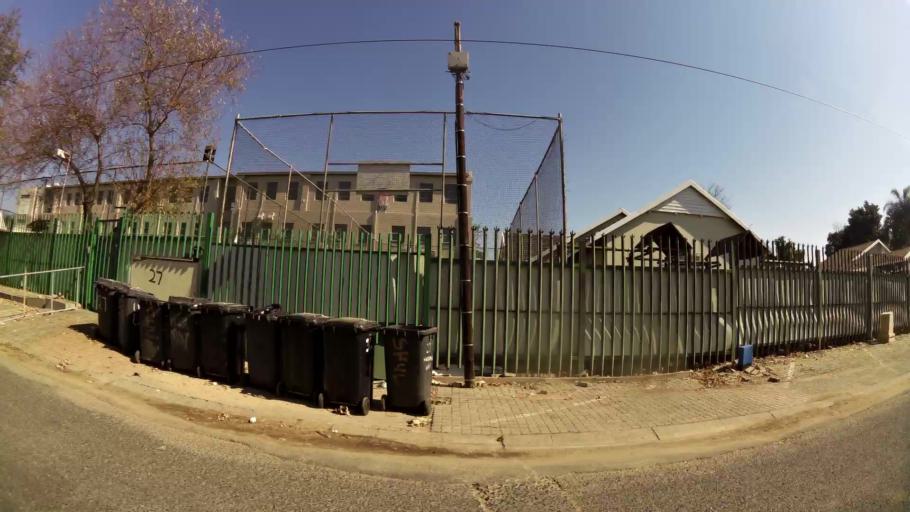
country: ZA
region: Gauteng
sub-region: City of Johannesburg Metropolitan Municipality
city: Johannesburg
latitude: -26.1460
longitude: 28.0990
